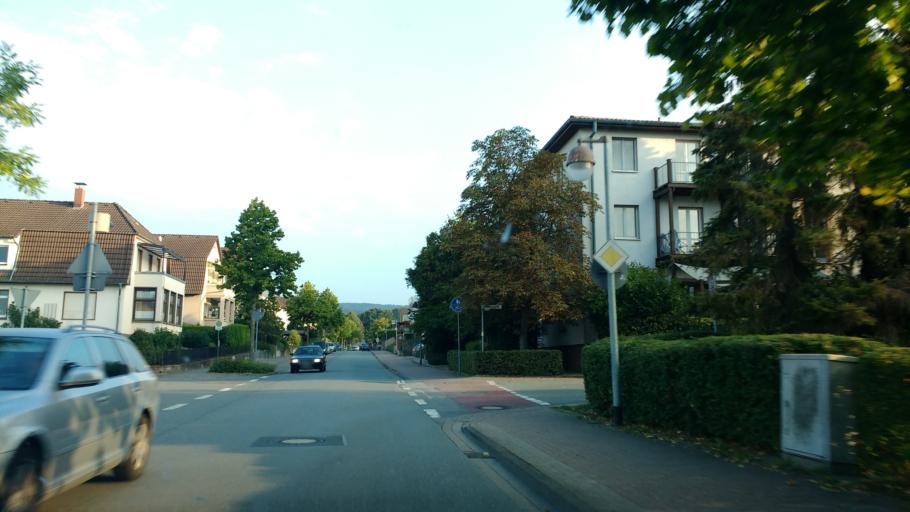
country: DE
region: Lower Saxony
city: Bad Pyrmont
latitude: 51.9789
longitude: 9.2675
